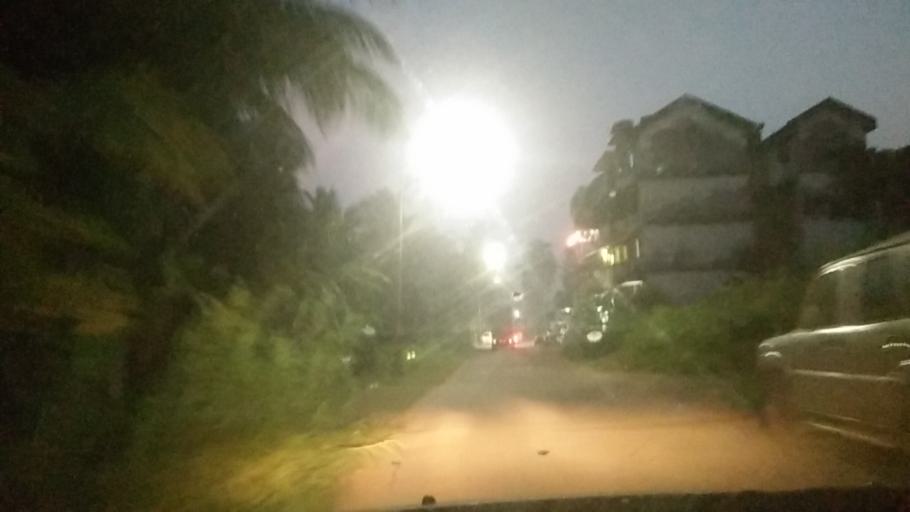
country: IN
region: Goa
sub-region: South Goa
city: Madgaon
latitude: 15.2645
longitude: 73.9647
